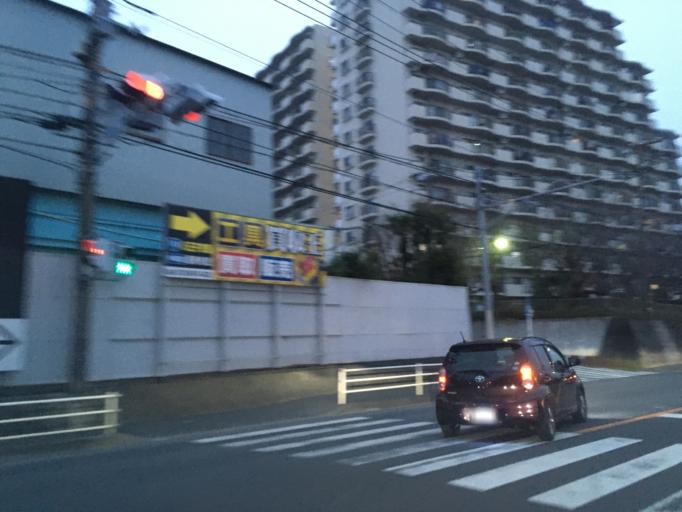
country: JP
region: Kanagawa
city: Minami-rinkan
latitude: 35.4932
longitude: 139.4629
